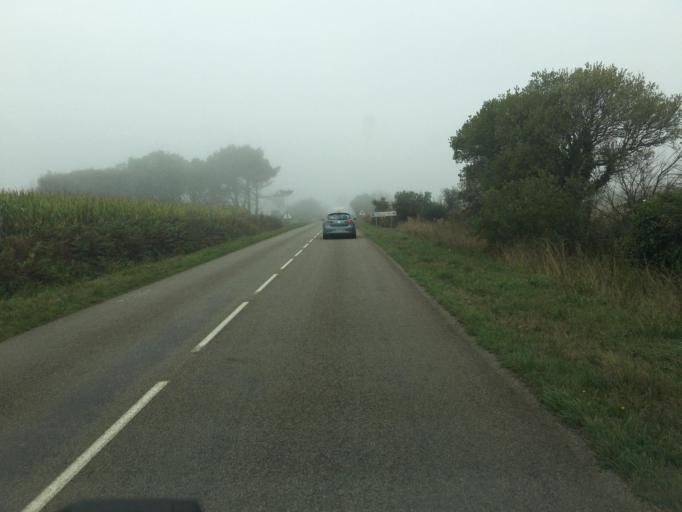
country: FR
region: Brittany
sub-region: Departement du Finistere
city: Plogoff
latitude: 48.0571
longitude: -4.6976
